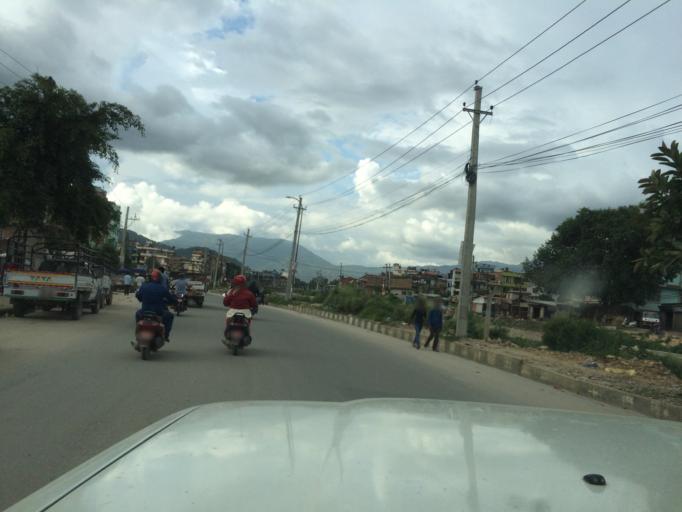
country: NP
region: Central Region
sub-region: Bagmati Zone
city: Kathmandu
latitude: 27.7025
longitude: 85.3019
